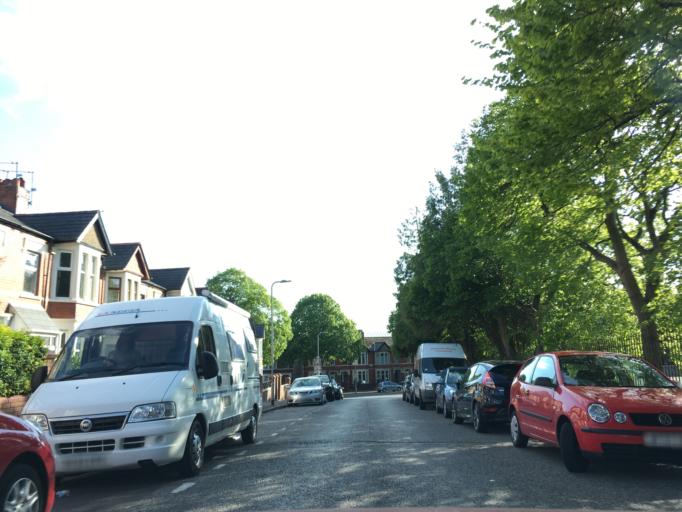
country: GB
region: Wales
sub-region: Cardiff
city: Cardiff
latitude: 51.4963
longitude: -3.1885
